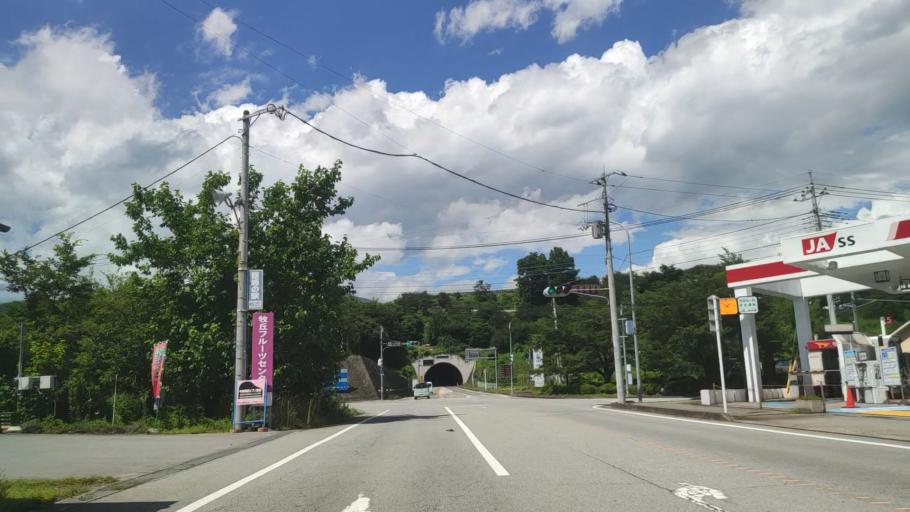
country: JP
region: Yamanashi
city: Enzan
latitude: 35.7418
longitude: 138.7076
